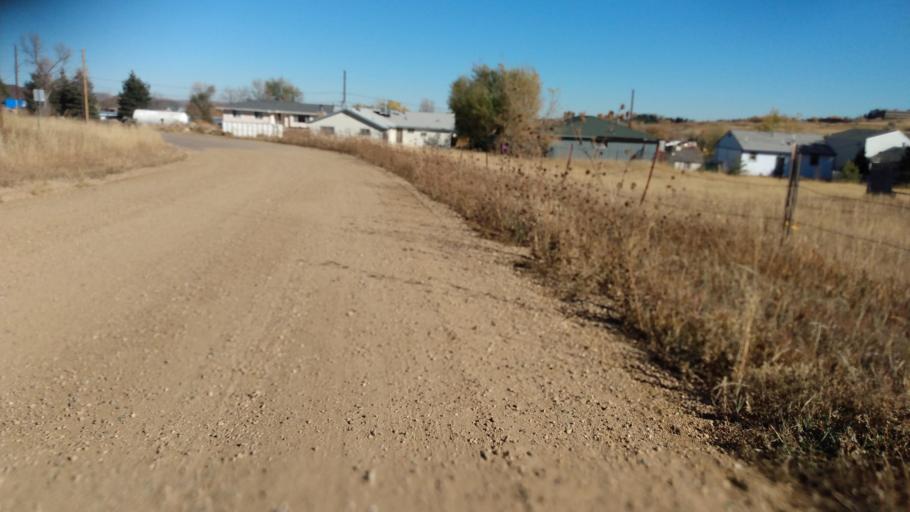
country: US
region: Colorado
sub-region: Boulder County
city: Superior
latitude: 39.9518
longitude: -105.1784
